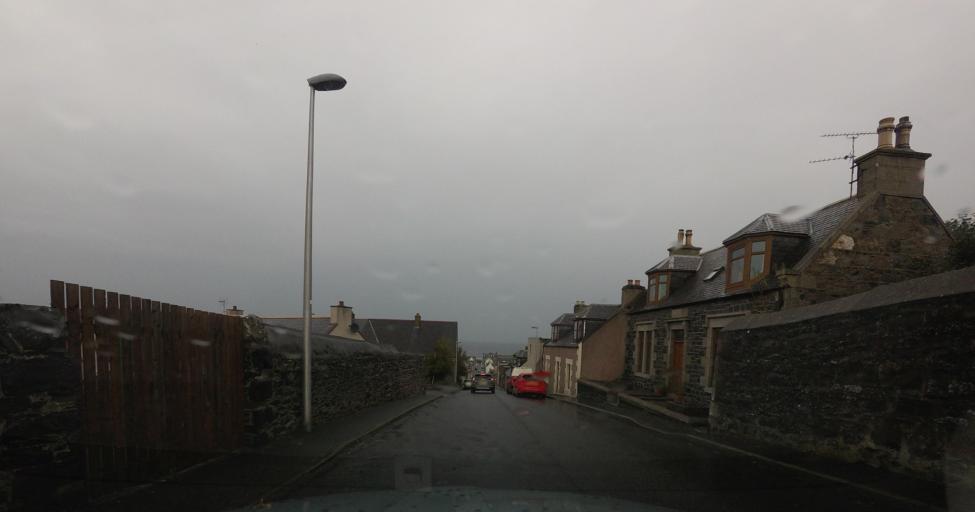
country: GB
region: Scotland
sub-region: Aberdeenshire
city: Macduff
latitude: 57.6672
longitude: -2.4995
